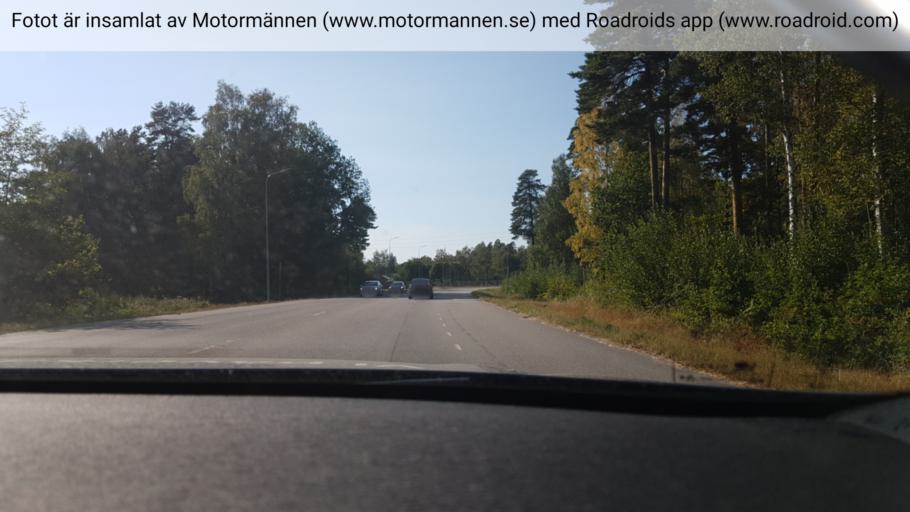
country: SE
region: Vaestra Goetaland
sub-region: Mariestads Kommun
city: Mariestad
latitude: 58.6946
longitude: 13.8115
